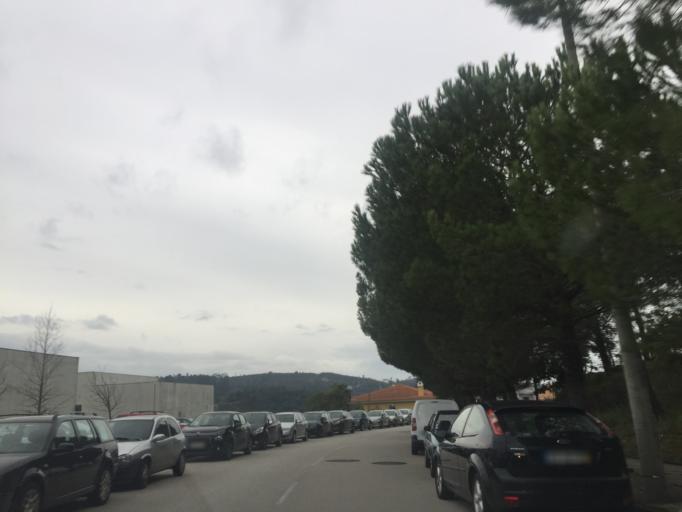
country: PT
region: Coimbra
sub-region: Coimbra
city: Coimbra
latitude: 40.1871
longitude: -8.4166
